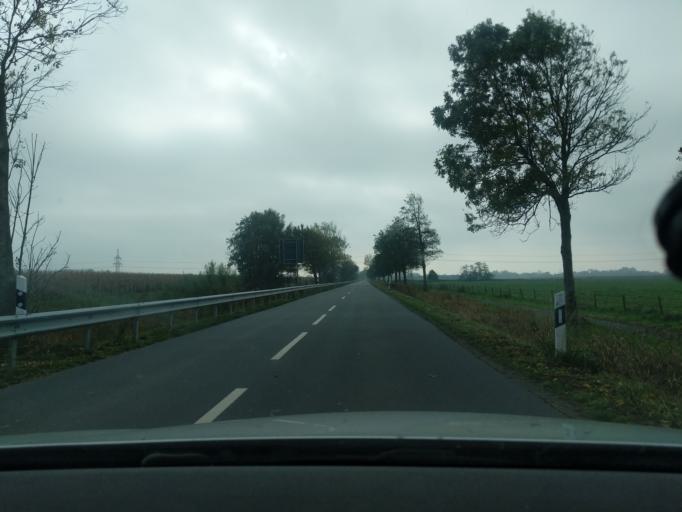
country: DE
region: Lower Saxony
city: Wanna
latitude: 53.8138
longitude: 8.7651
